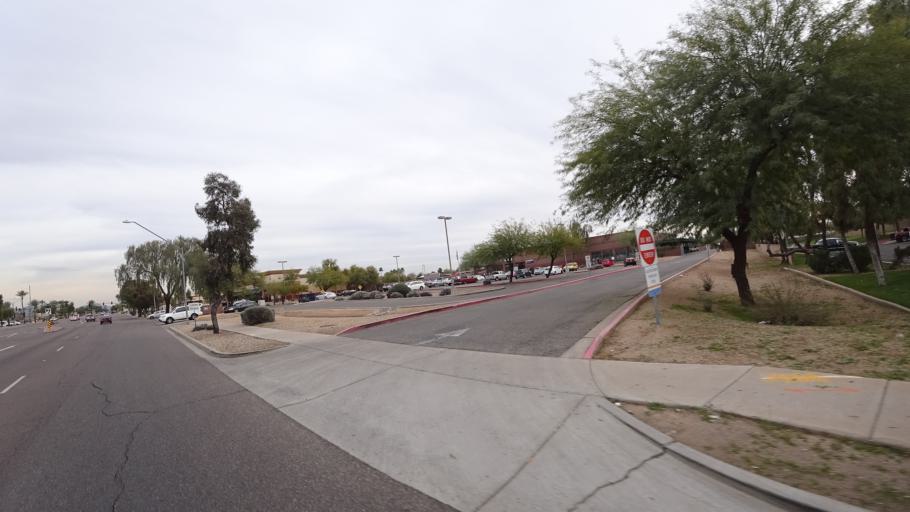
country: US
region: Arizona
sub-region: Maricopa County
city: Glendale
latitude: 33.5818
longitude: -112.1884
